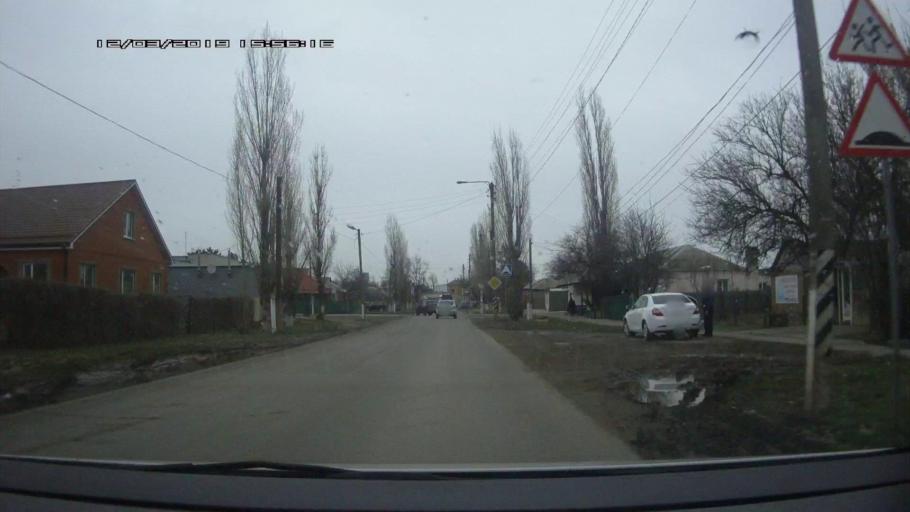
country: RU
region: Rostov
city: Novobataysk
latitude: 46.8998
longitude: 39.7810
